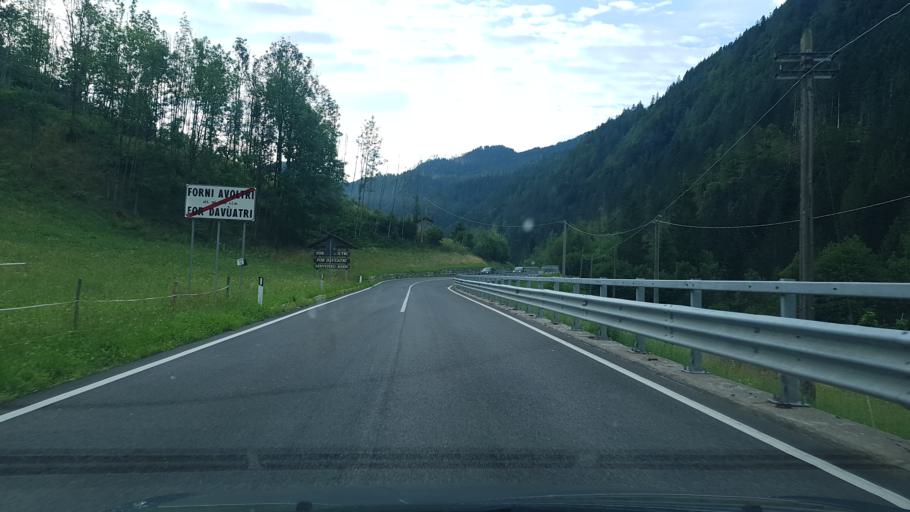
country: IT
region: Friuli Venezia Giulia
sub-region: Provincia di Udine
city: Forni Avoltri
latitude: 46.5835
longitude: 12.7821
